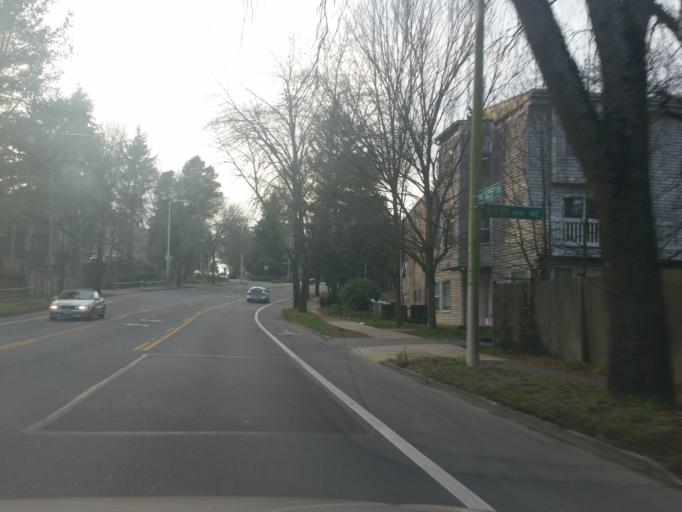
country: US
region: Washington
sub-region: King County
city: Shoreline
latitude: 47.7195
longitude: -122.3160
